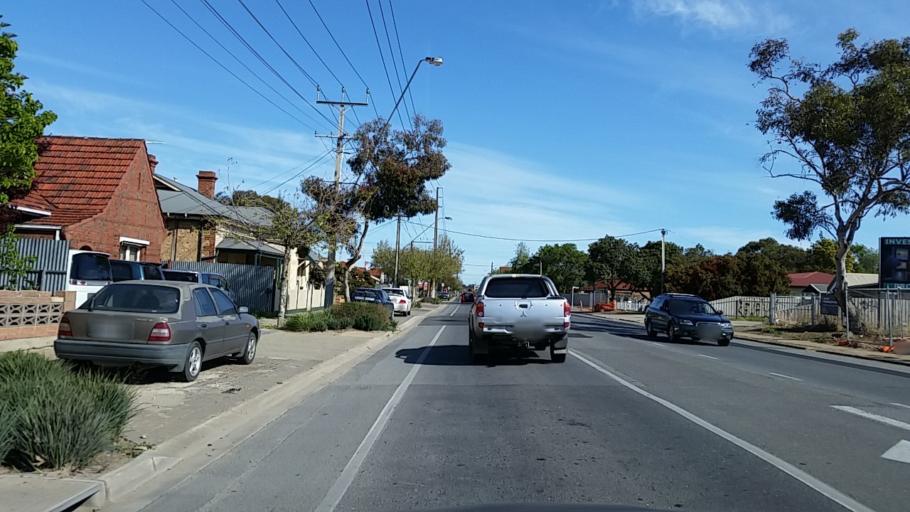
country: AU
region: South Australia
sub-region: Prospect
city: Prospect
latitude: -34.8778
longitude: 138.5844
